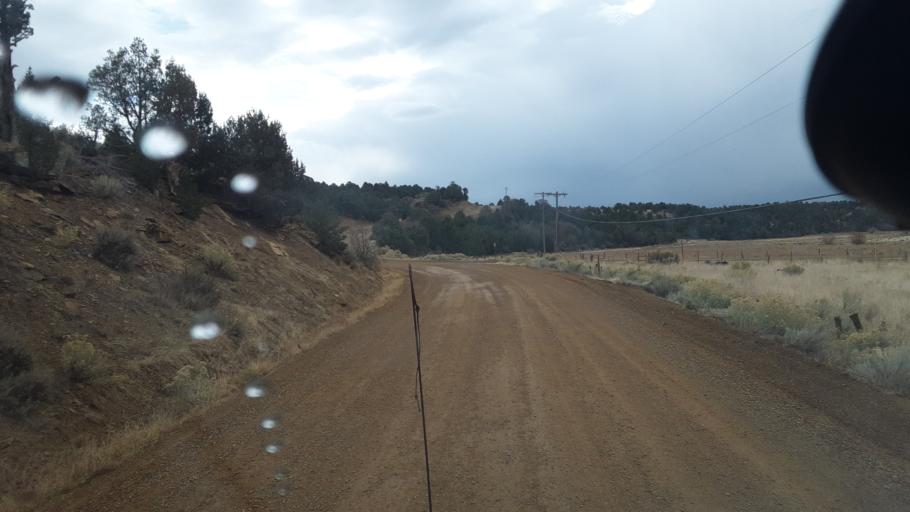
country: US
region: Colorado
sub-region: Montezuma County
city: Mancos
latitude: 37.2021
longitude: -108.1386
